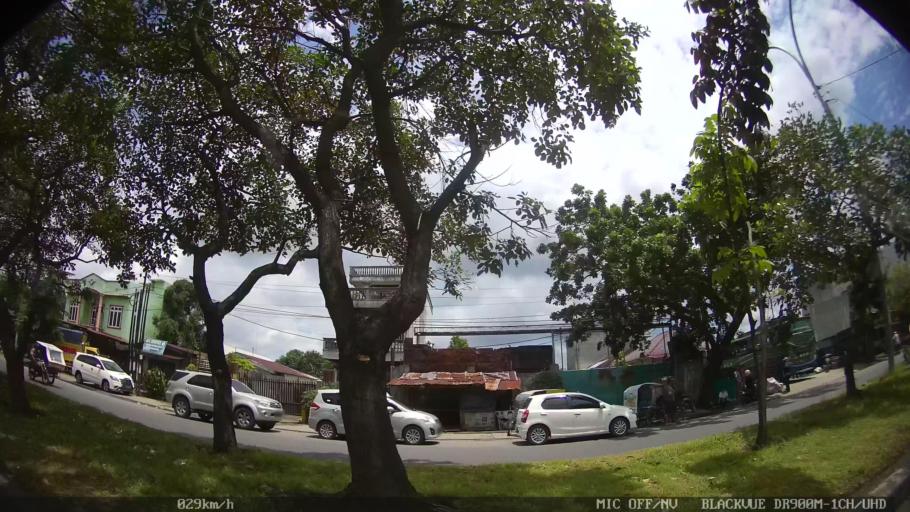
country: ID
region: North Sumatra
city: Medan
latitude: 3.5973
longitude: 98.7257
